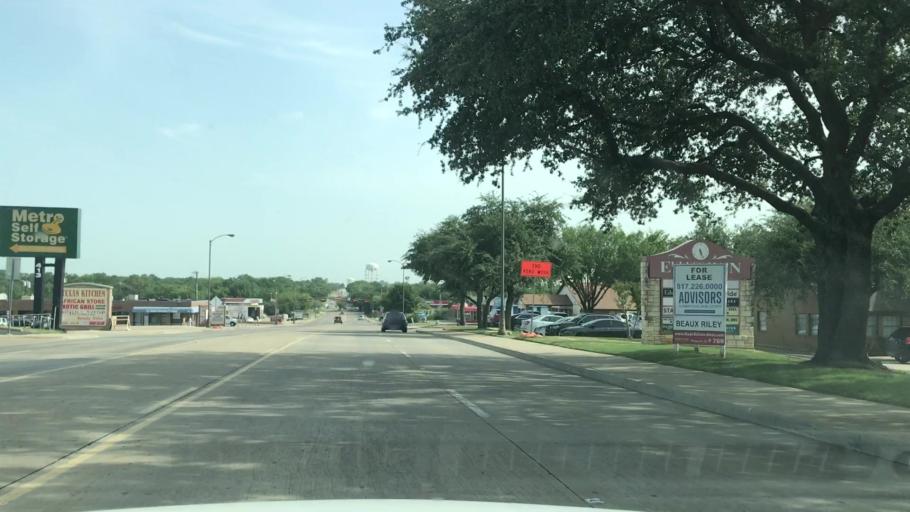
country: US
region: Texas
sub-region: Tarrant County
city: Euless
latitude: 32.8420
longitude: -97.0826
